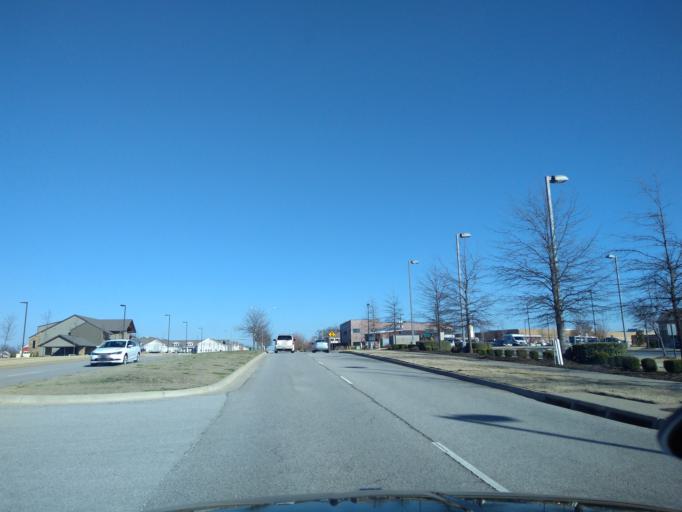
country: US
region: Arkansas
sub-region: Washington County
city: Johnson
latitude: 36.1177
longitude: -94.1592
